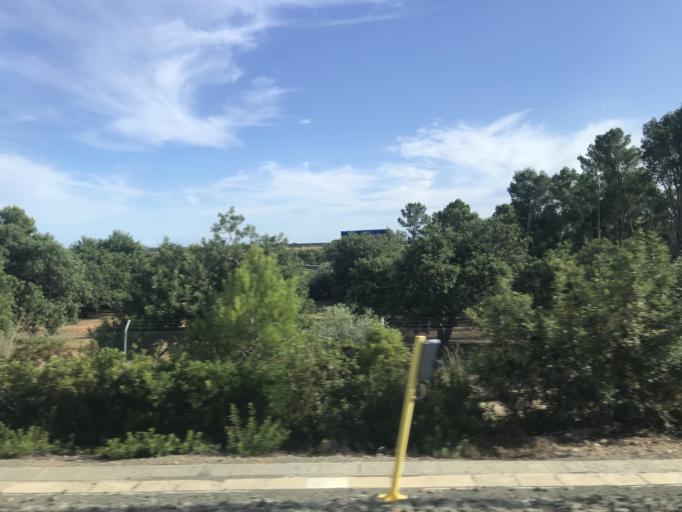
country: ES
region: Catalonia
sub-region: Provincia de Tarragona
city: Vilanova d'Escornalbou
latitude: 41.0420
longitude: 0.9597
